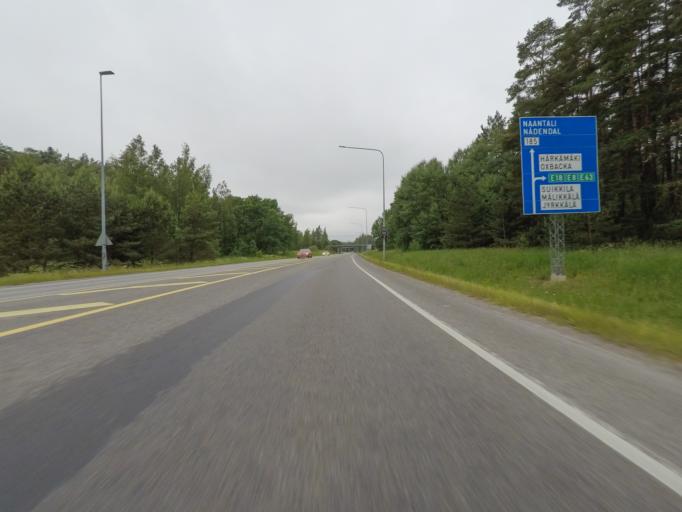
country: FI
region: Varsinais-Suomi
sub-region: Turku
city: Raisio
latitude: 60.4602
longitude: 22.2073
